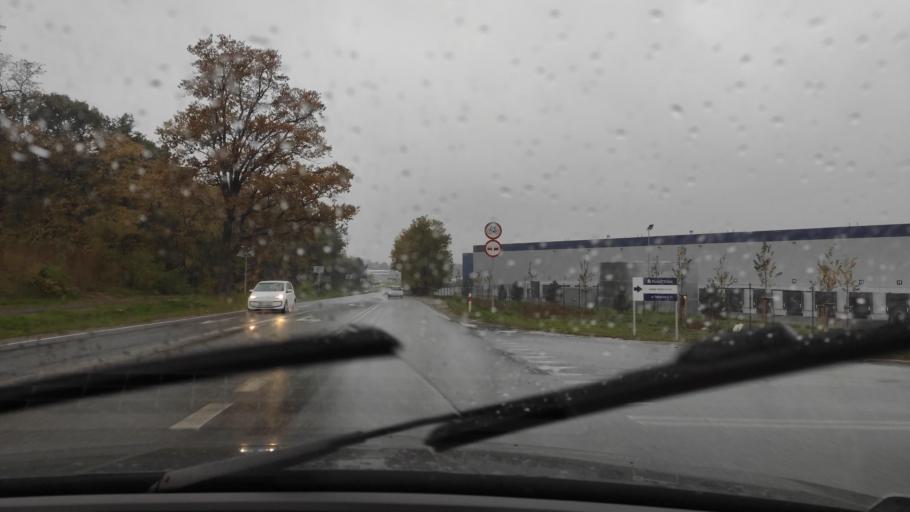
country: PL
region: Greater Poland Voivodeship
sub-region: Powiat poznanski
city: Daszewice
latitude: 52.3267
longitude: 17.0429
